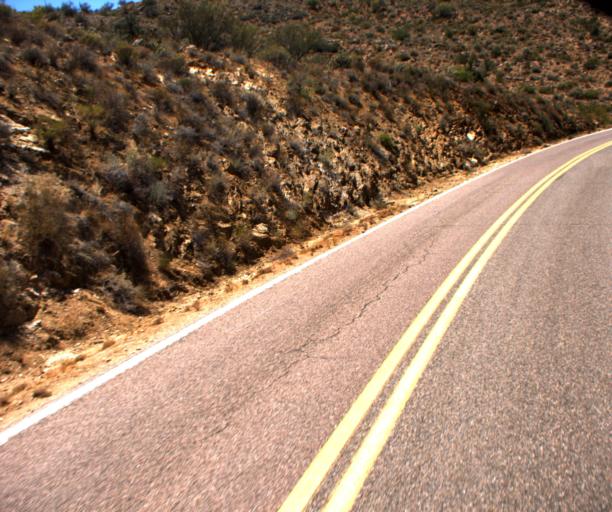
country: US
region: Arizona
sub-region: Yavapai County
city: Bagdad
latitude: 34.4573
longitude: -113.0151
